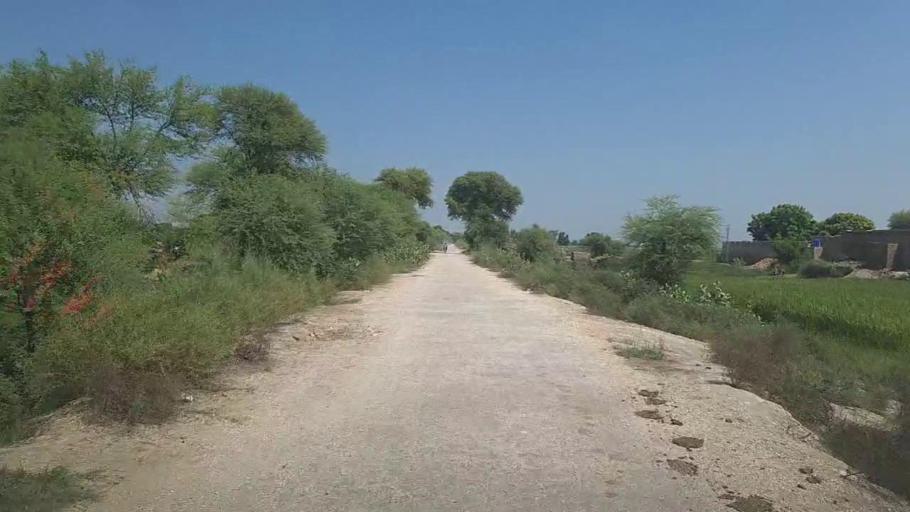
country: PK
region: Sindh
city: Kandhkot
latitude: 28.3017
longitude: 69.2404
